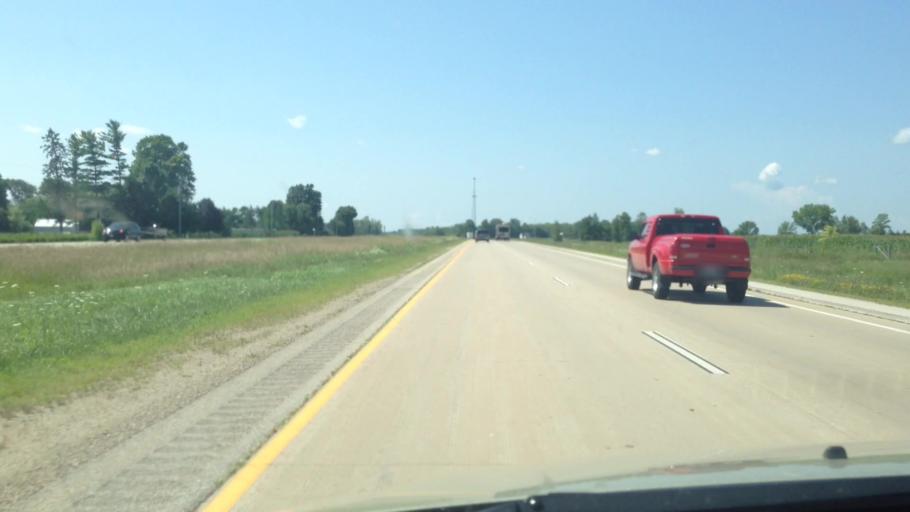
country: US
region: Wisconsin
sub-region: Marinette County
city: Peshtigo
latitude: 45.0089
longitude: -87.8458
